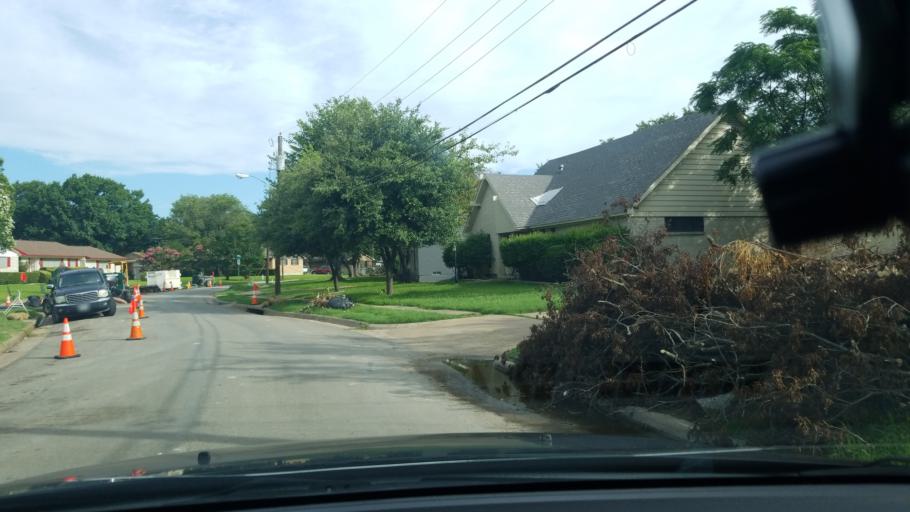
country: US
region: Texas
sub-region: Dallas County
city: Balch Springs
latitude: 32.7573
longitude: -96.6687
